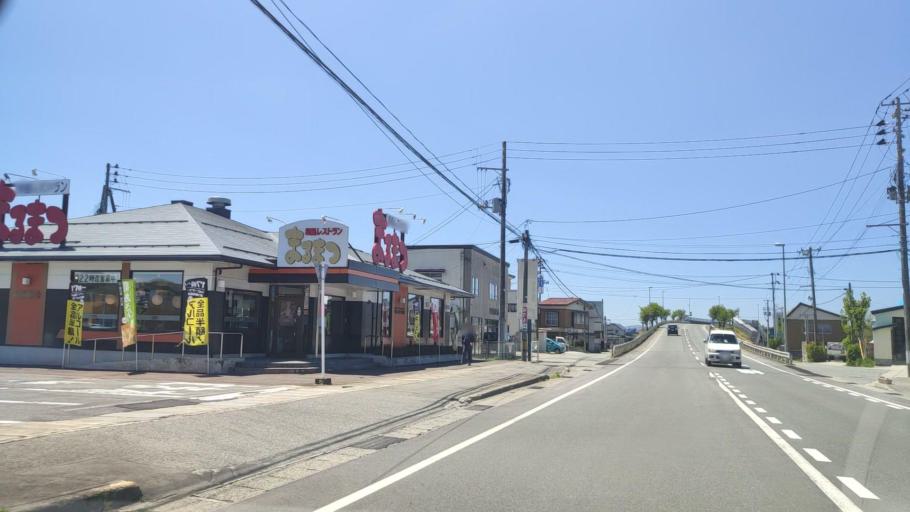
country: JP
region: Yamagata
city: Shinjo
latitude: 38.7712
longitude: 140.3079
